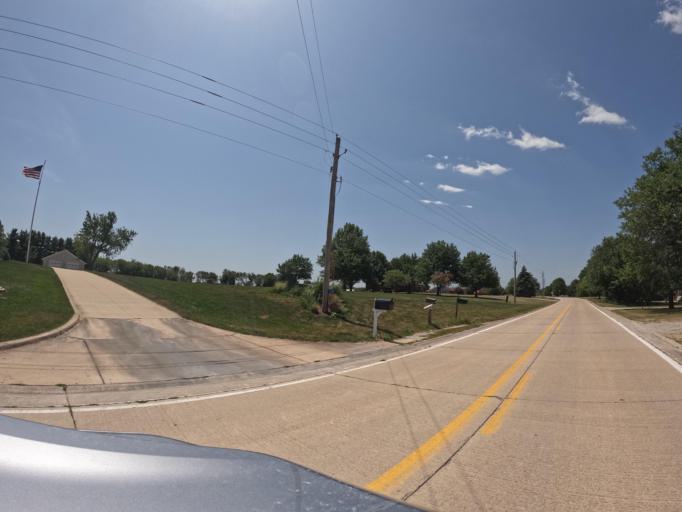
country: US
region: Iowa
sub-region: Henry County
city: Mount Pleasant
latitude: 40.9769
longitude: -91.5855
